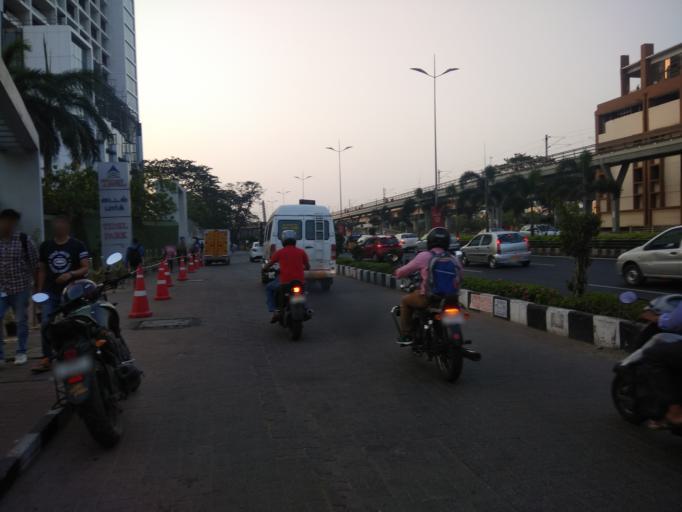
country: IN
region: Tamil Nadu
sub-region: Chennai
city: Gandhi Nagar
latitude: 12.9901
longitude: 80.2507
